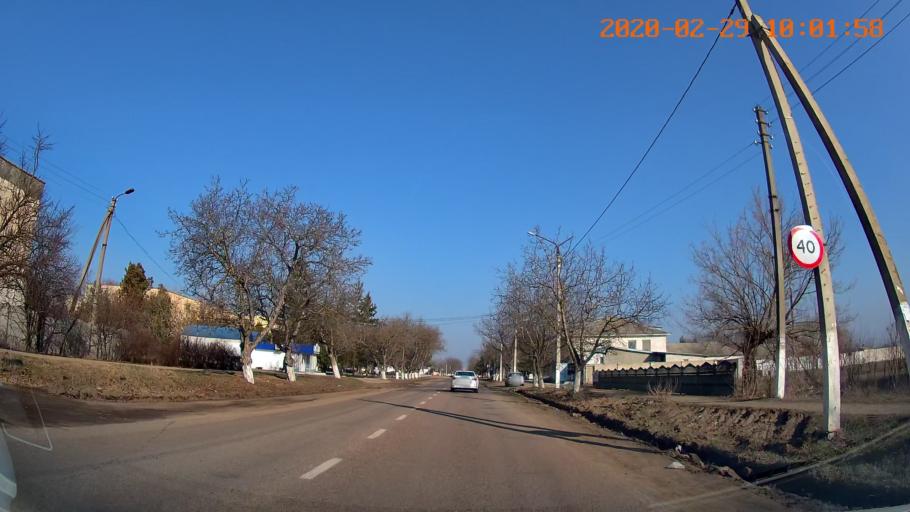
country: MD
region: Telenesti
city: Slobozia
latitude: 46.7792
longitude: 29.6841
